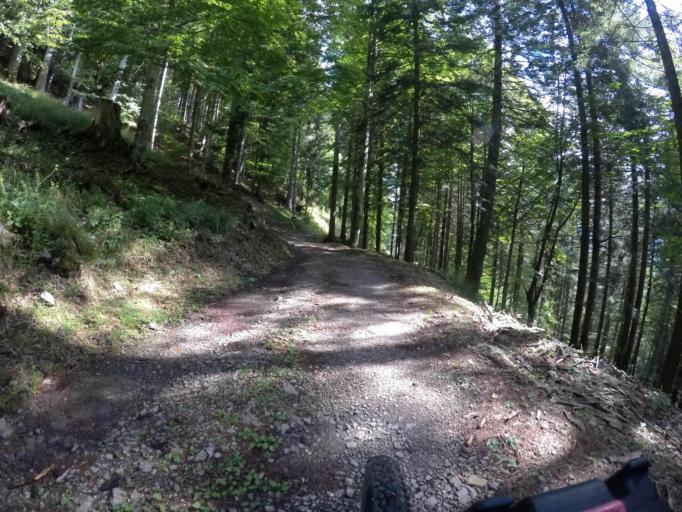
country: IT
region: Friuli Venezia Giulia
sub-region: Provincia di Udine
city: Paularo
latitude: 46.5056
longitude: 13.1780
